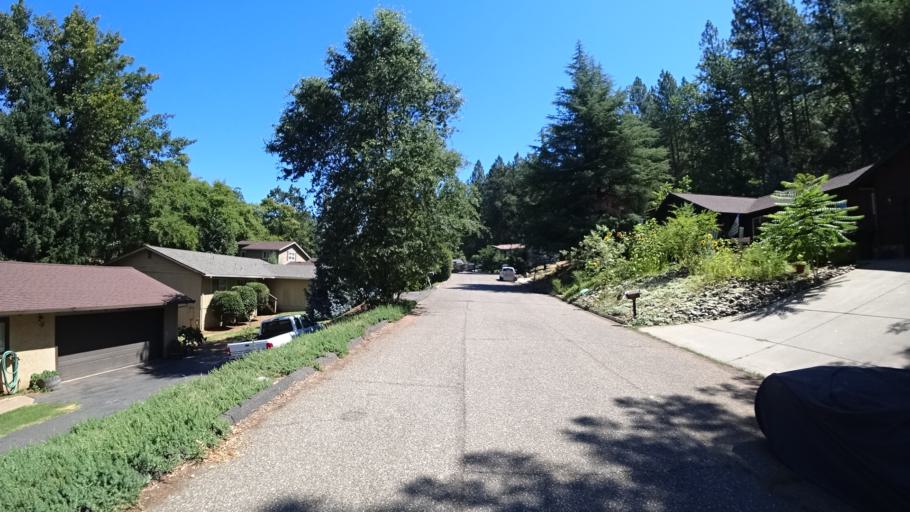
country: US
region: California
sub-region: Calaveras County
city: Murphys
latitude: 38.1423
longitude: -120.4510
